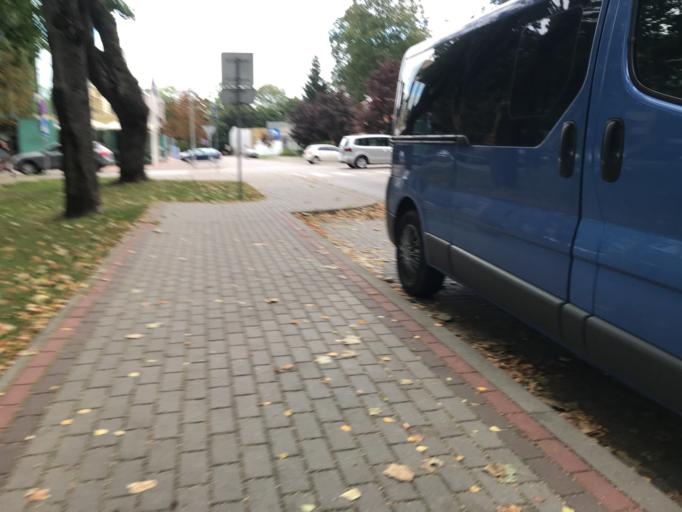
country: LT
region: Alytaus apskritis
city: Druskininkai
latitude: 54.0180
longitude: 23.9751
